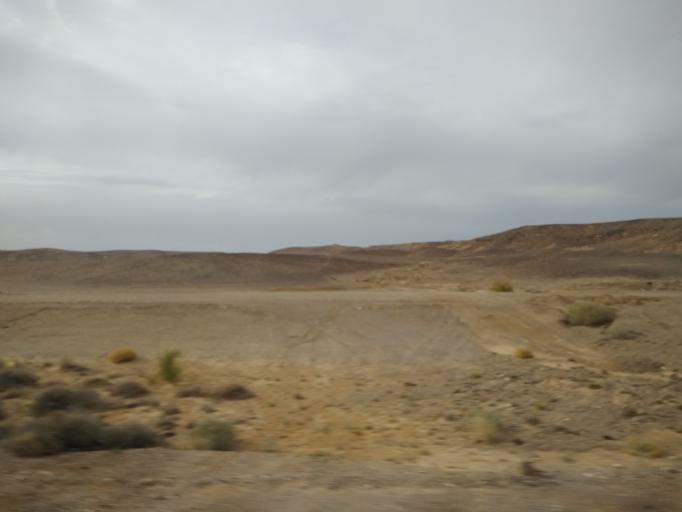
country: IL
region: Southern District
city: Eilat
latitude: 29.9118
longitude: 34.8763
